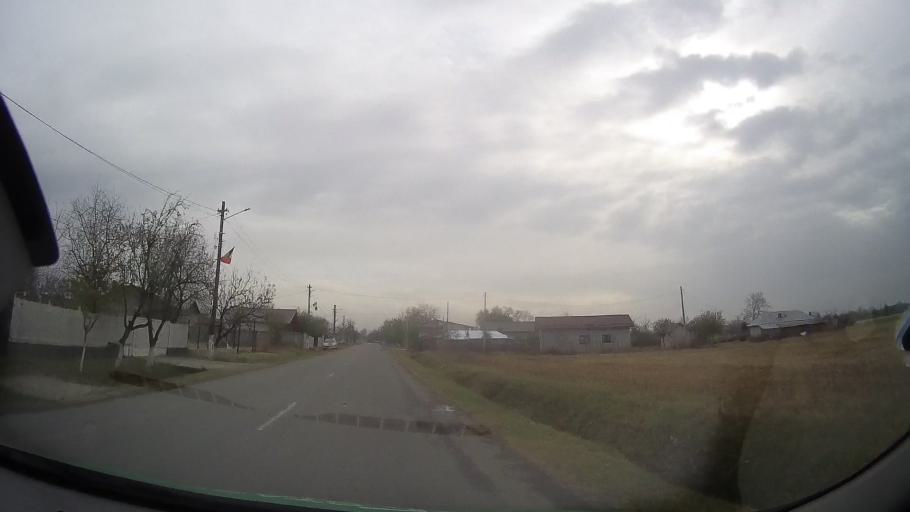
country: RO
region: Prahova
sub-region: Comuna Dumbrava
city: Dumbrava
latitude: 44.8785
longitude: 26.1829
